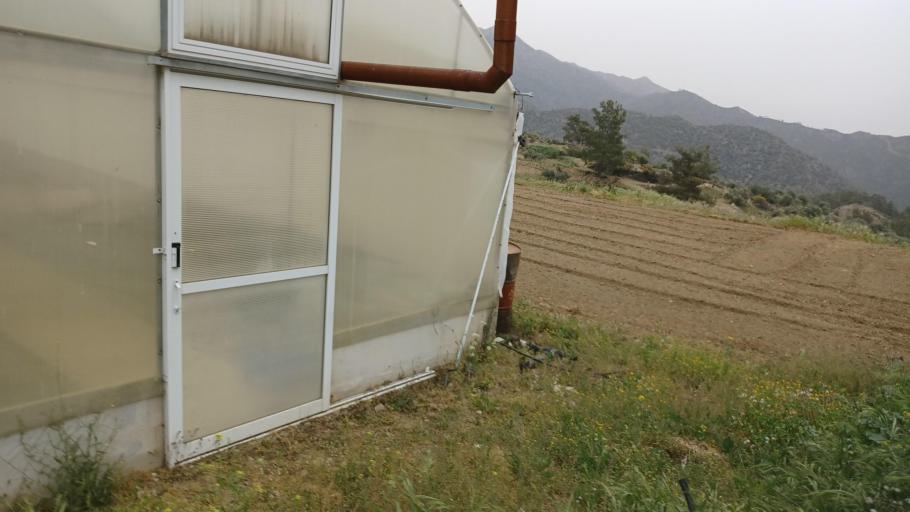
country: CY
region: Limassol
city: Parekklisha
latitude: 34.8611
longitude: 33.0960
